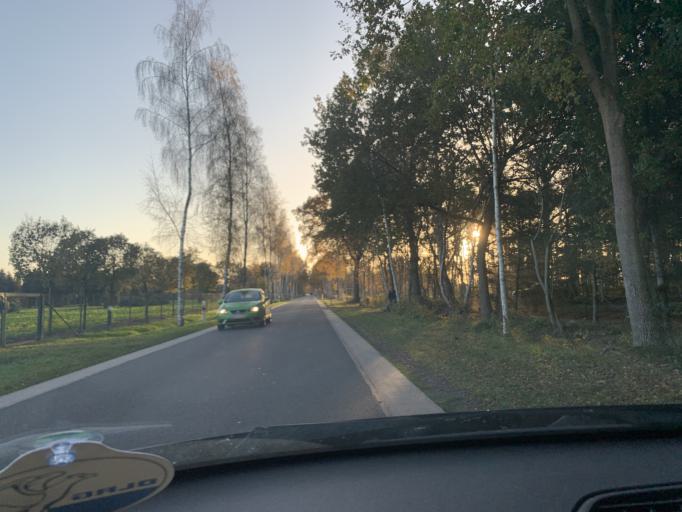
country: DE
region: Lower Saxony
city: Bad Zwischenahn
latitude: 53.1628
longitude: 8.0612
